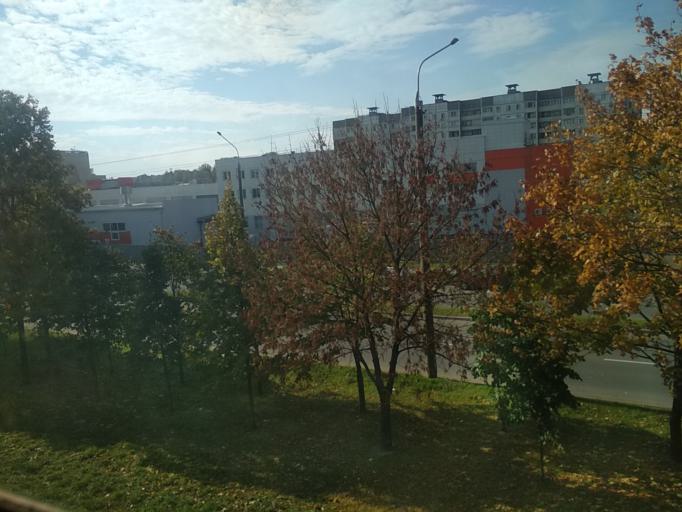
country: BY
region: Minsk
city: Minsk
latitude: 53.8788
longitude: 27.5629
